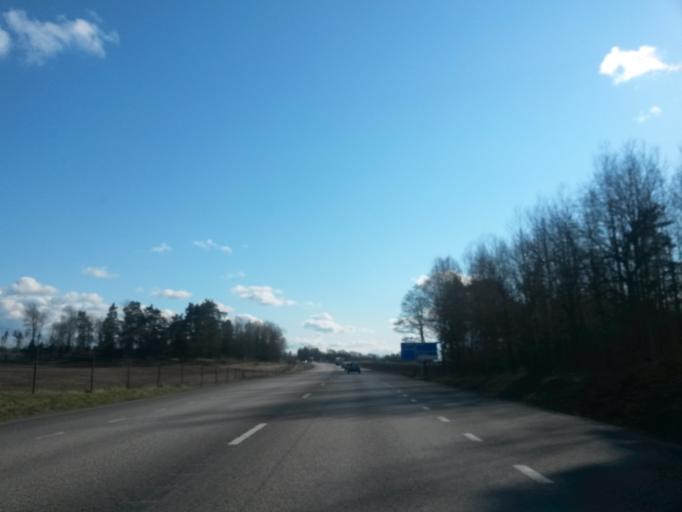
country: SE
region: Vaestra Goetaland
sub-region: Vargarda Kommun
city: Vargarda
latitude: 58.1511
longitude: 12.8680
